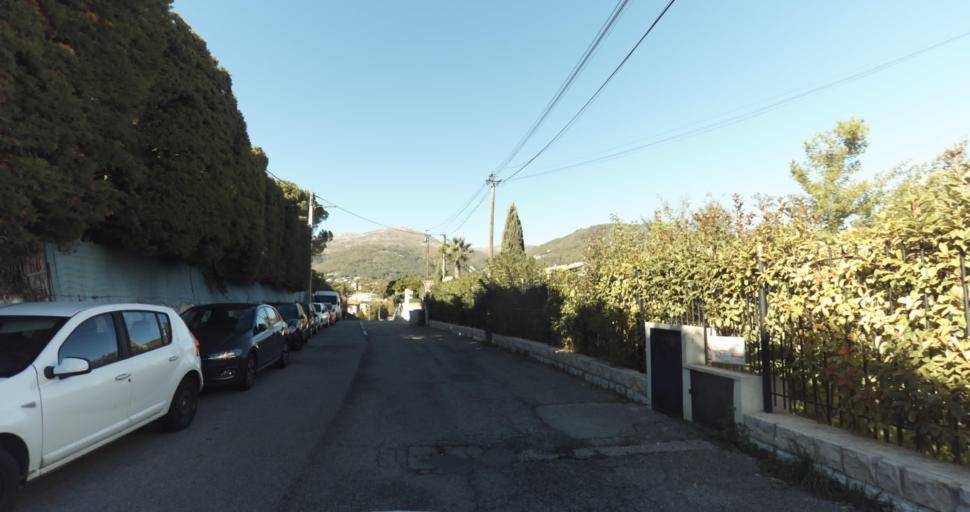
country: FR
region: Provence-Alpes-Cote d'Azur
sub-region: Departement des Alpes-Maritimes
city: Vence
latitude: 43.7195
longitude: 7.1096
